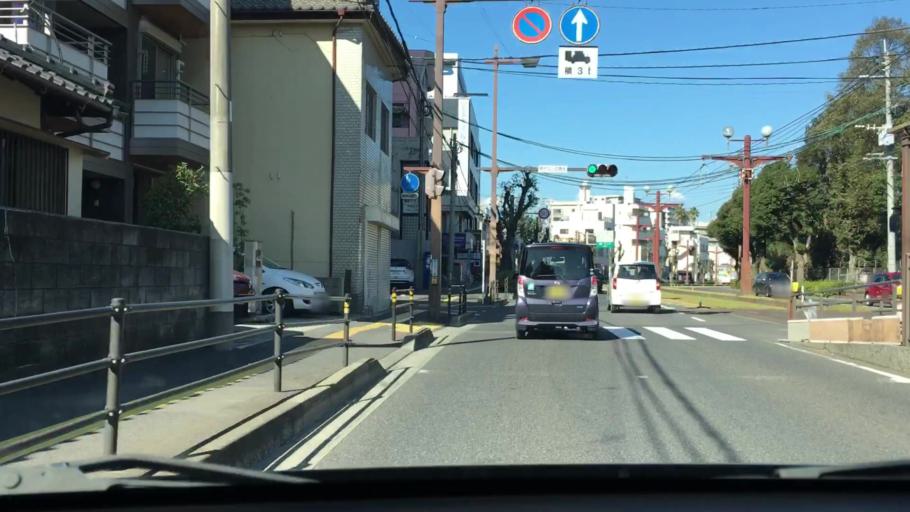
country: JP
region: Kagoshima
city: Kagoshima-shi
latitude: 31.5667
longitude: 130.5427
